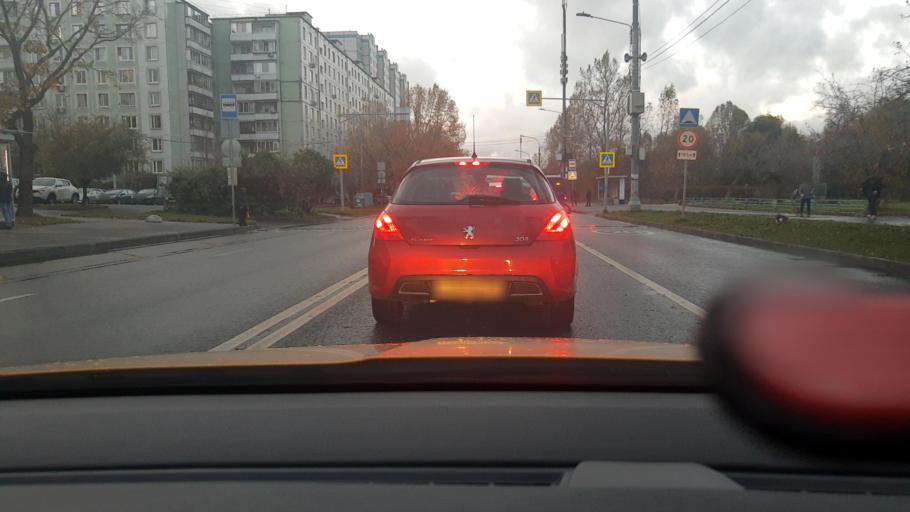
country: RU
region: Moscow
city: Strogino
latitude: 55.8126
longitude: 37.4108
